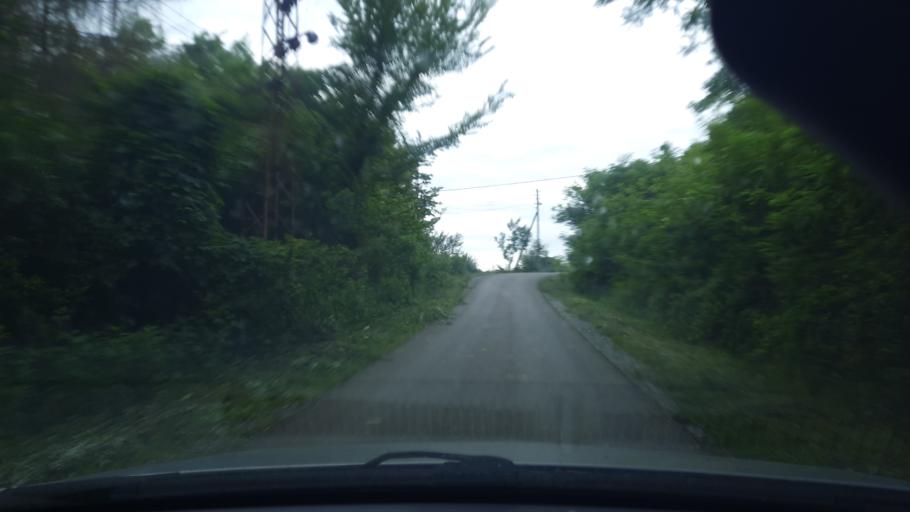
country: RS
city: Jarebice
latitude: 44.4845
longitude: 19.4777
